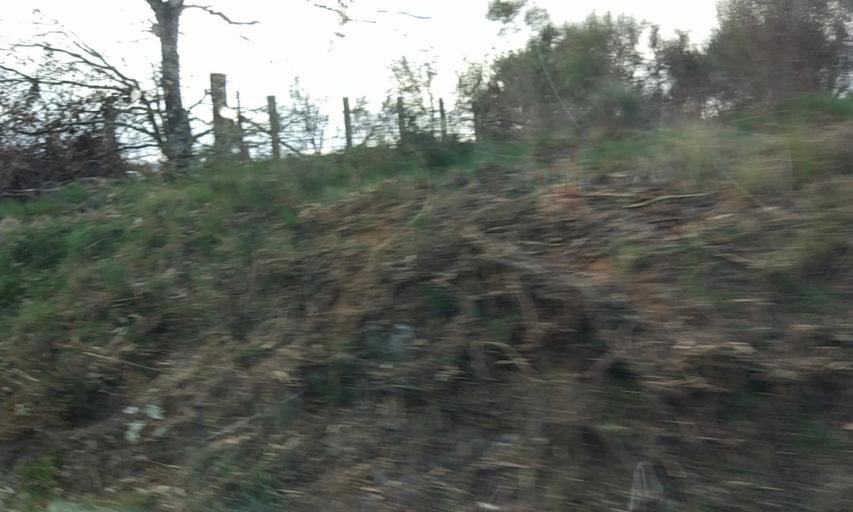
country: ES
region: Castille and Leon
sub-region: Provincia de Salamanca
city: Villasrubias
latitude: 40.3445
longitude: -6.6373
